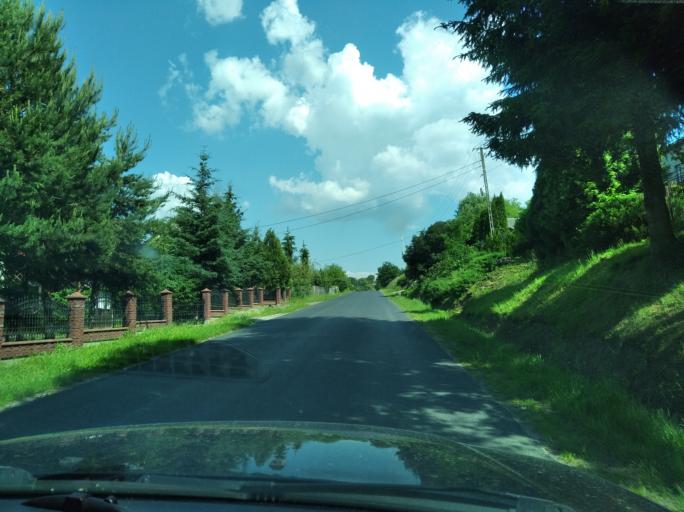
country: PL
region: Subcarpathian Voivodeship
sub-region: Powiat jaroslawski
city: Jodlowka
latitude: 49.9098
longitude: 22.4817
